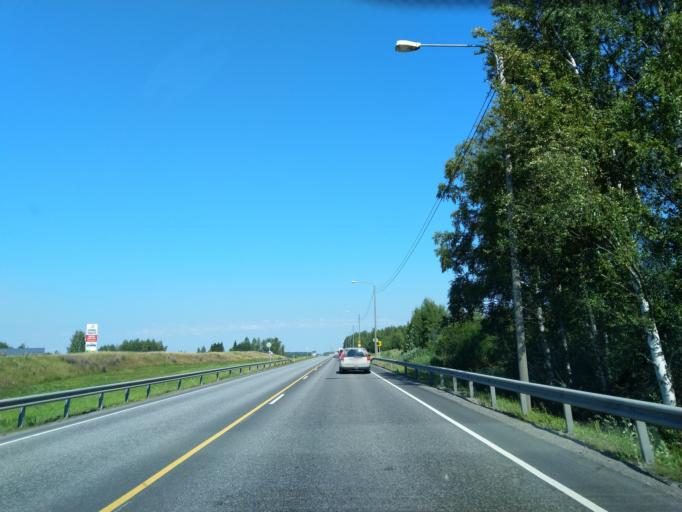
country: FI
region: Satakunta
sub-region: Pori
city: Nakkila
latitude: 61.3637
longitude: 21.9916
